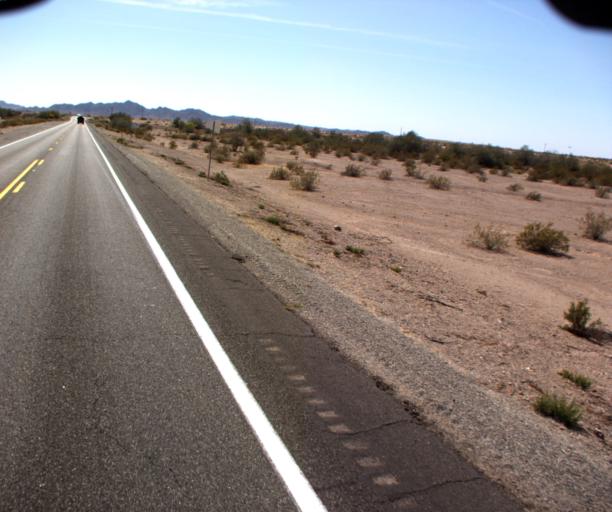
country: US
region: Arizona
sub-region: Yuma County
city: Fortuna Foothills
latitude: 32.8626
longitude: -114.3581
